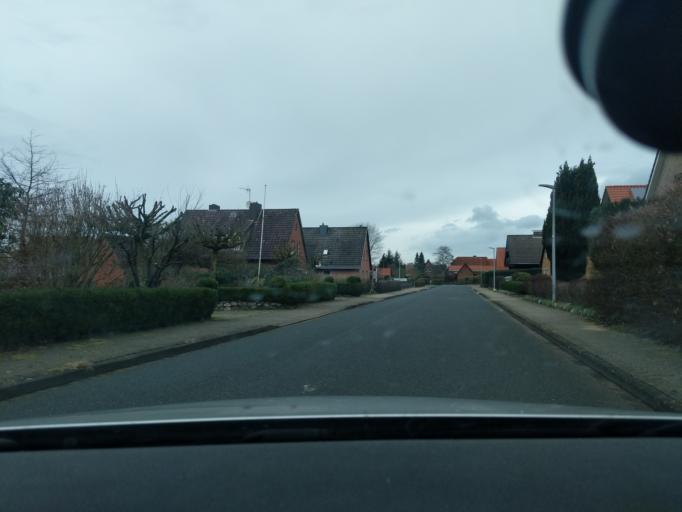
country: DE
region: Lower Saxony
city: Bremervorde
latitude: 53.4640
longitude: 9.1931
